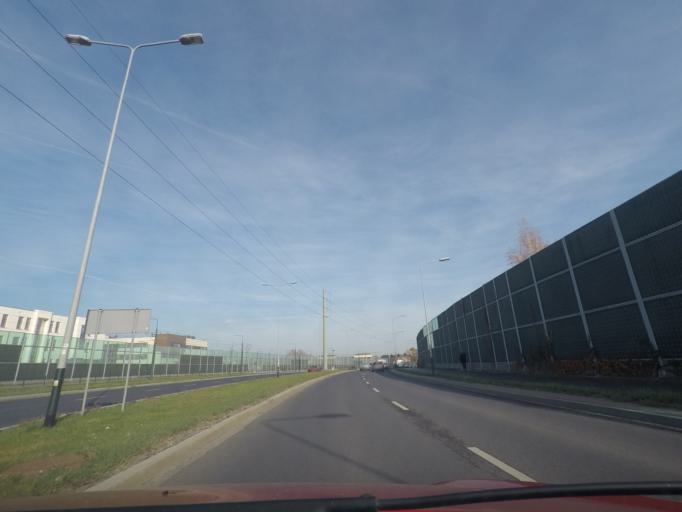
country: PL
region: Lesser Poland Voivodeship
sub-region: Krakow
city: Sidzina
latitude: 50.0253
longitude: 19.9028
